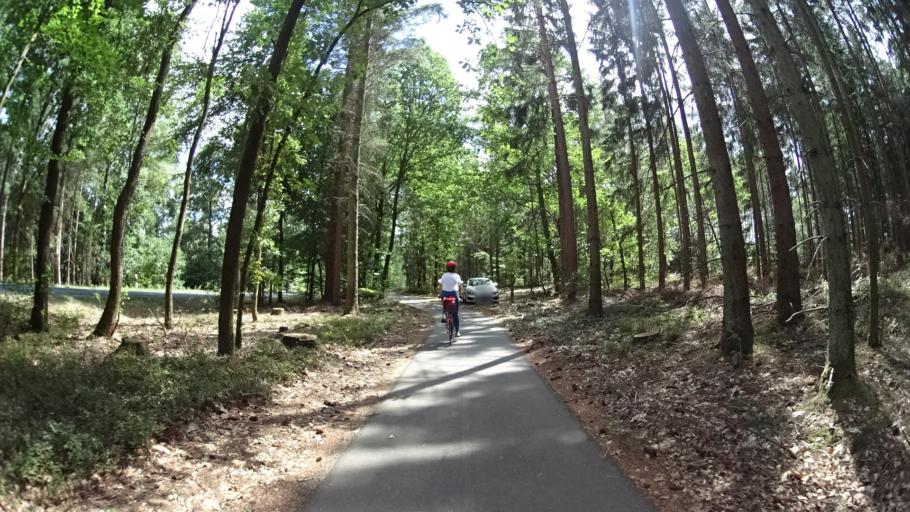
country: DE
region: Lower Saxony
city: Undeloh
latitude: 53.2044
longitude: 9.9607
